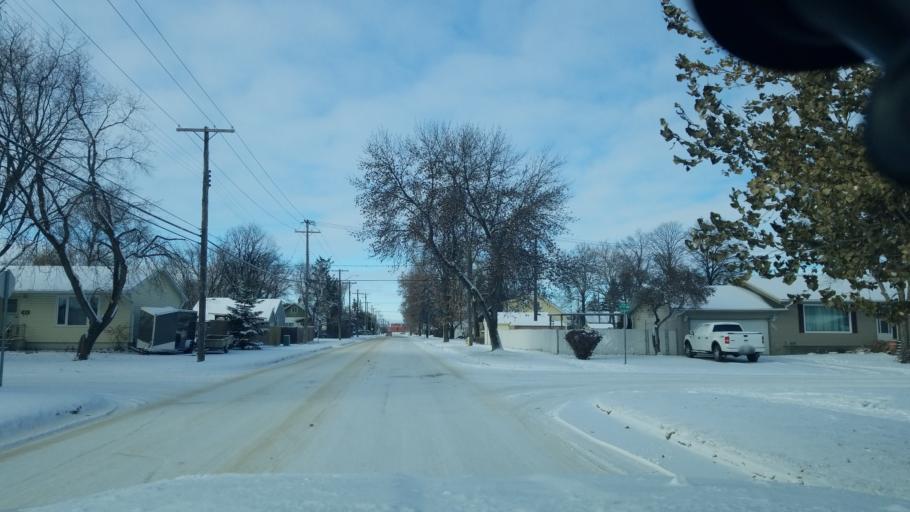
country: CA
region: Manitoba
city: Portage la Prairie
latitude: 49.9810
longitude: -98.2977
